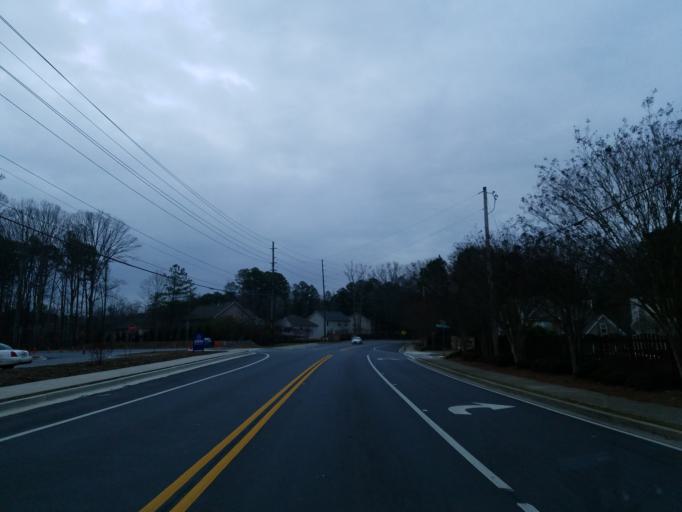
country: US
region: Georgia
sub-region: Cobb County
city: Acworth
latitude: 34.0440
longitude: -84.6562
